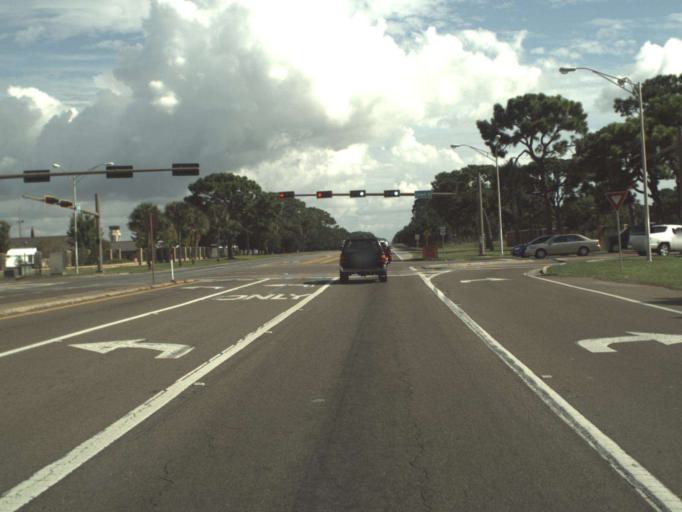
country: US
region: Florida
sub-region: Bay County
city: Tyndall Air Force Base
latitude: 30.0708
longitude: -85.5914
